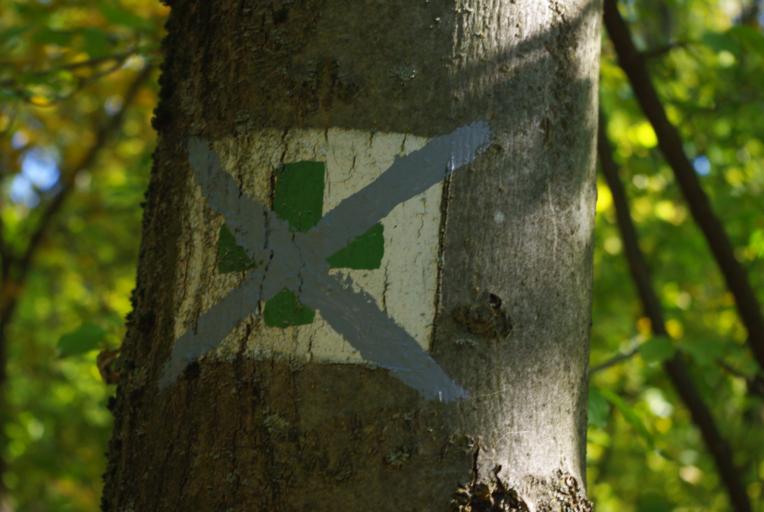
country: HU
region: Pest
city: Budakeszi
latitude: 47.5333
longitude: 18.9251
